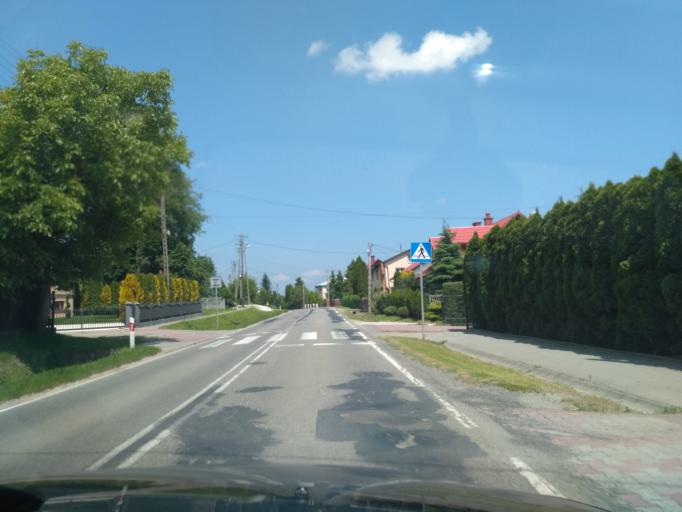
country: PL
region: Subcarpathian Voivodeship
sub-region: Powiat lancucki
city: Albigowa
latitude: 50.0188
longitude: 22.2249
